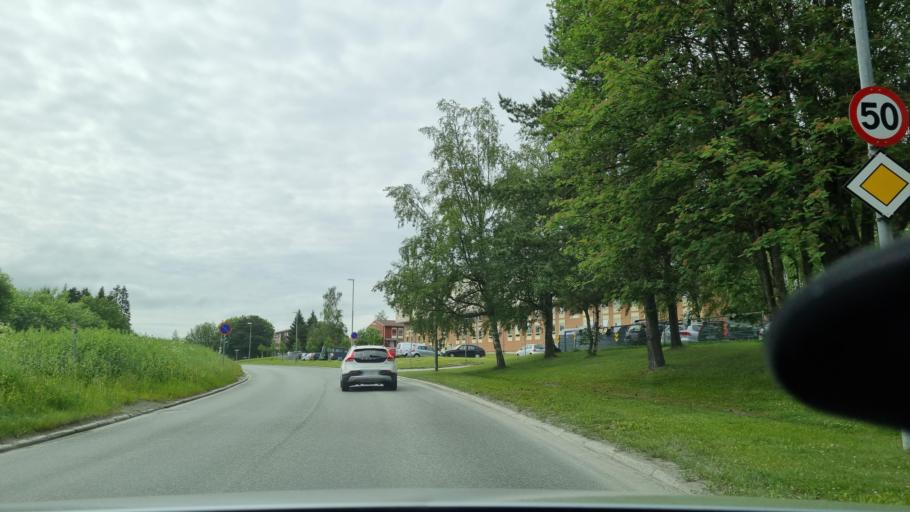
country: NO
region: Sor-Trondelag
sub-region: Melhus
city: Melhus
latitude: 63.3464
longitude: 10.3443
